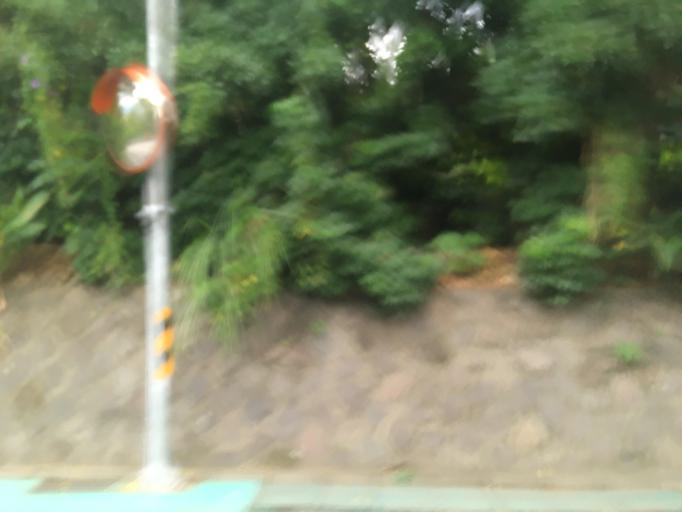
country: TW
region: Taipei
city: Taipei
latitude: 25.1346
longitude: 121.5288
